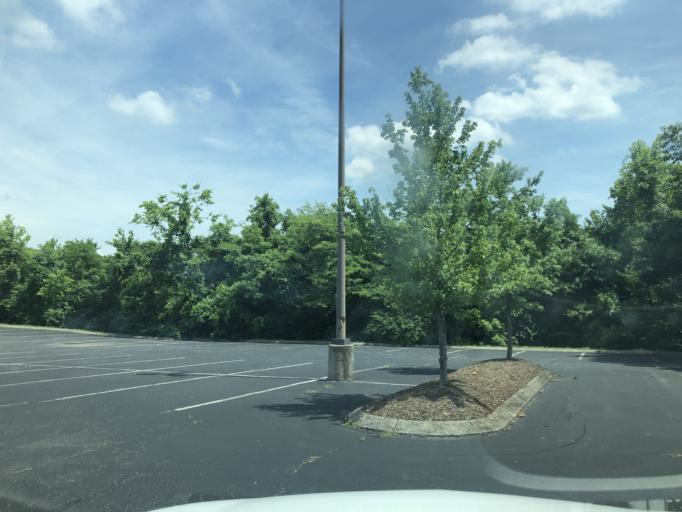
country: US
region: Tennessee
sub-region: Rutherford County
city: La Vergne
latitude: 36.0374
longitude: -86.6404
